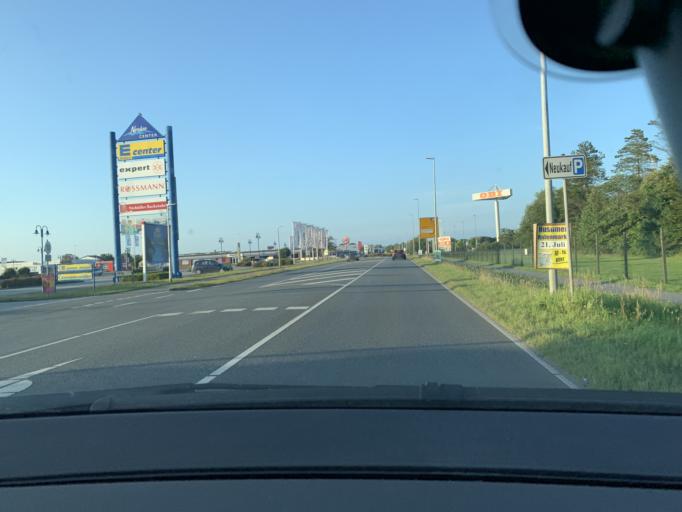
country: DE
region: Schleswig-Holstein
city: Husum
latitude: 54.4886
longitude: 9.0795
